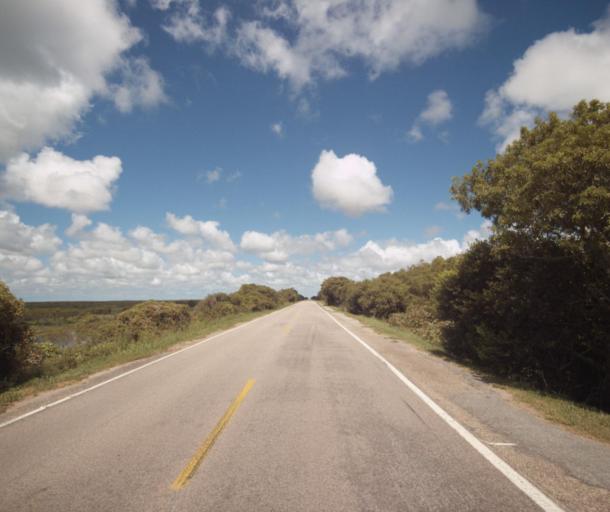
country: BR
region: Rio Grande do Sul
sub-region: Arroio Grande
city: Arroio Grande
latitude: -32.5481
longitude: -52.5447
